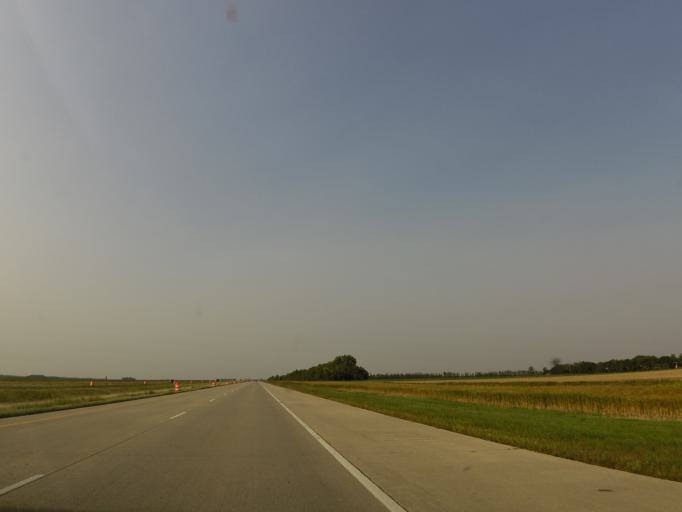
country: US
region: North Dakota
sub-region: Cass County
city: Horace
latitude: 46.5838
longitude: -96.8232
